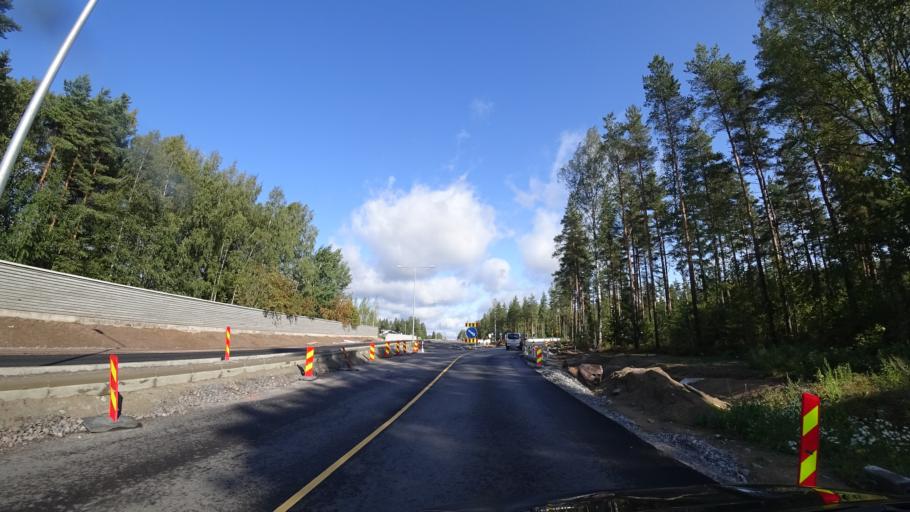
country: FI
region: Uusimaa
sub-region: Helsinki
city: Tuusula
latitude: 60.4098
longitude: 25.0051
